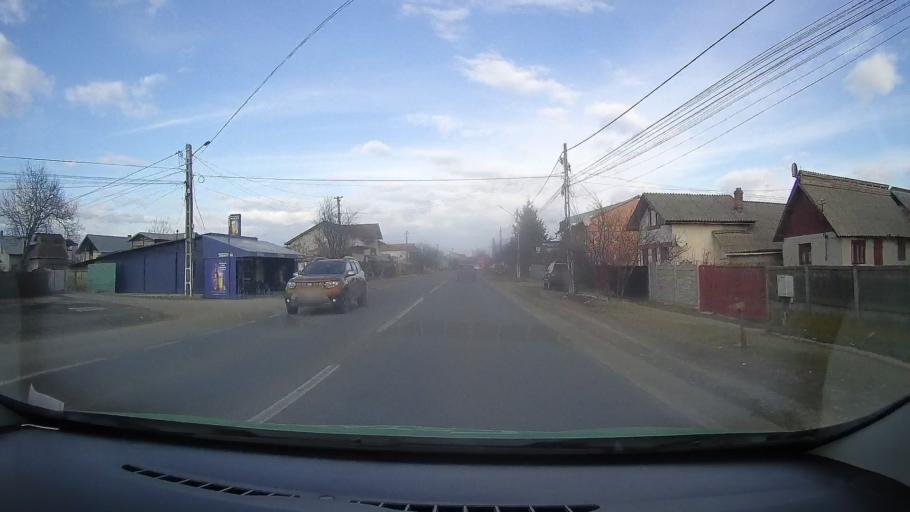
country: RO
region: Dambovita
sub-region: Comuna Ulmi
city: Viisoara
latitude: 44.8902
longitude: 25.4359
